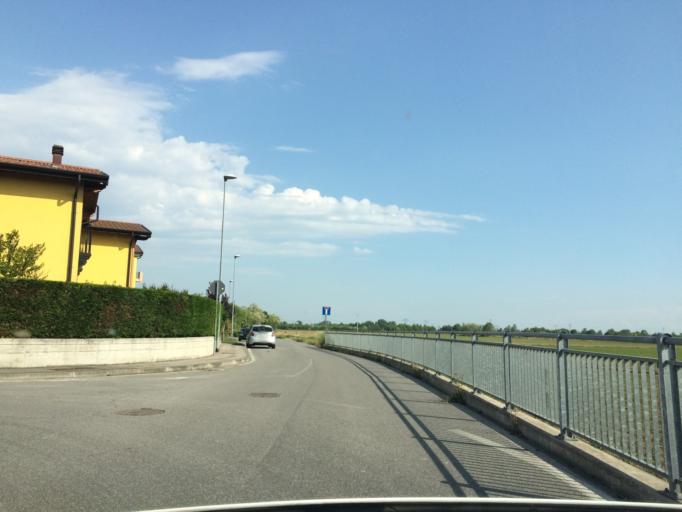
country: IT
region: Lombardy
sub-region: Provincia di Brescia
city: Flero
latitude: 45.4826
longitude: 10.1825
